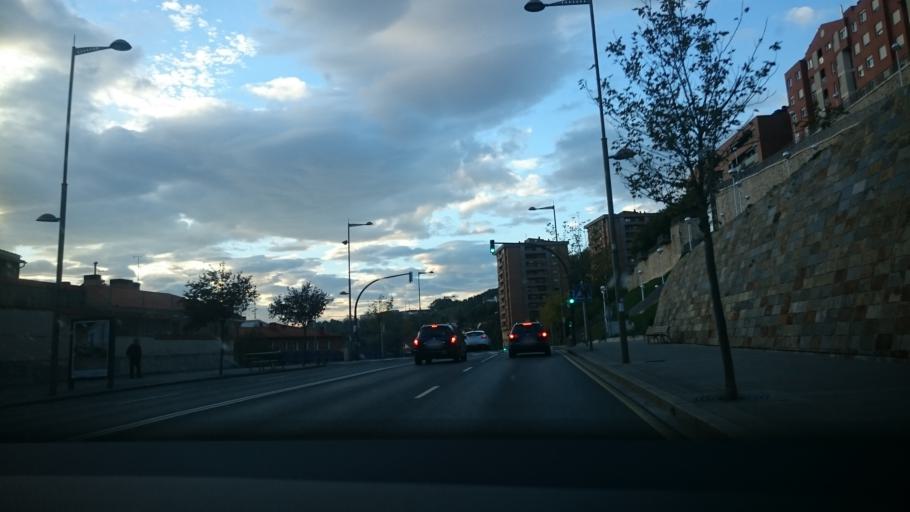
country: ES
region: Basque Country
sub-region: Bizkaia
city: Bilbao
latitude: 43.2688
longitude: -2.9203
